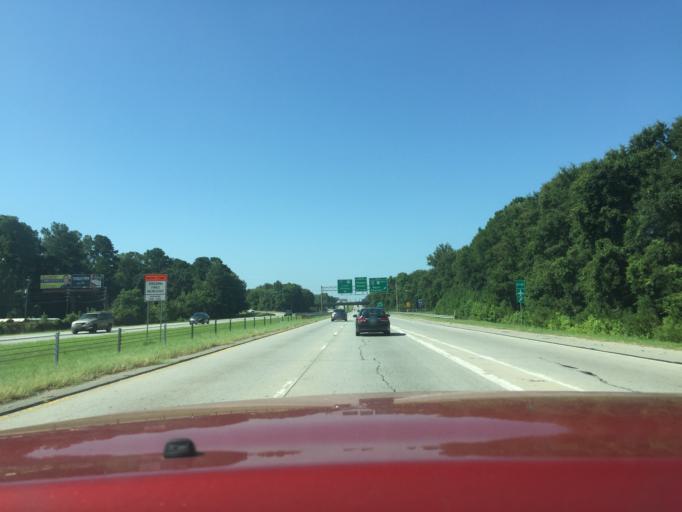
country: US
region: Georgia
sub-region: Chatham County
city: Savannah
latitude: 32.0765
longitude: -81.1333
